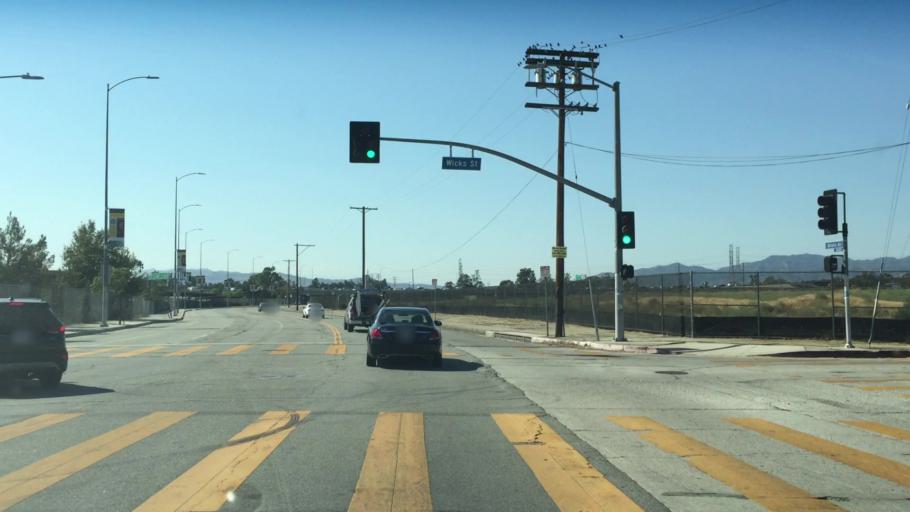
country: US
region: California
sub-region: Los Angeles County
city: Van Nuys
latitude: 34.2242
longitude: -118.4071
